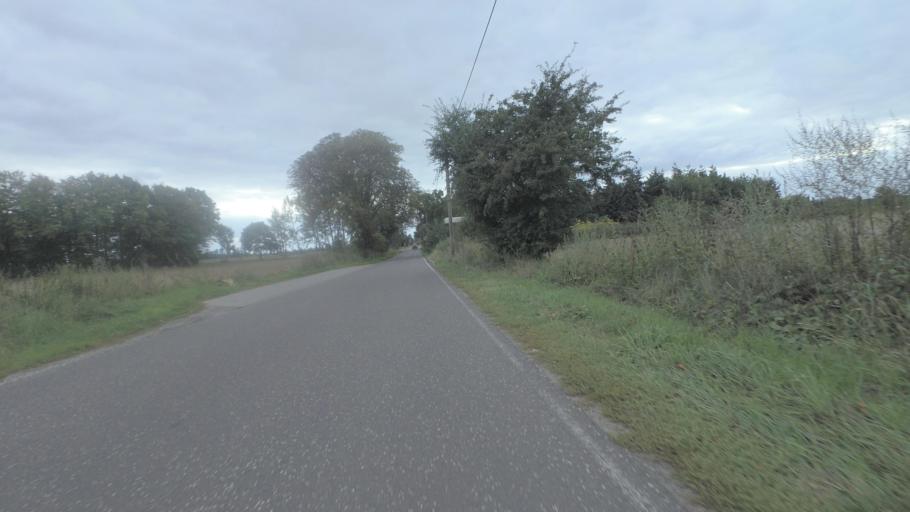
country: DE
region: Brandenburg
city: Neuenhagen
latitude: 52.5701
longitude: 13.6631
